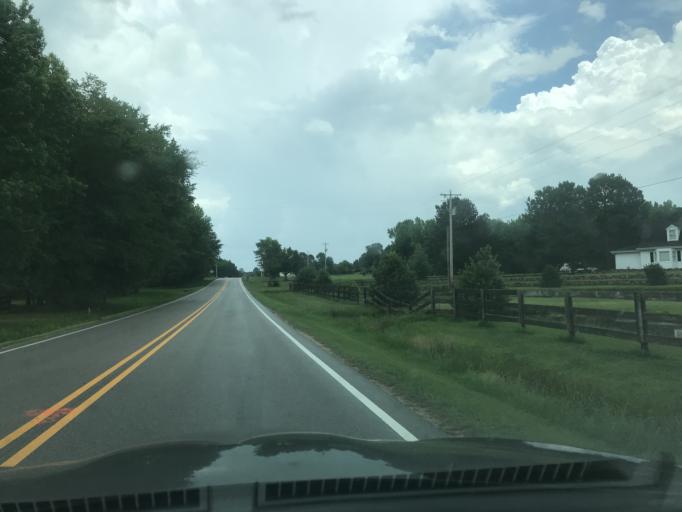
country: US
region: North Carolina
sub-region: Wake County
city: Knightdale
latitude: 35.8395
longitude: -78.5008
